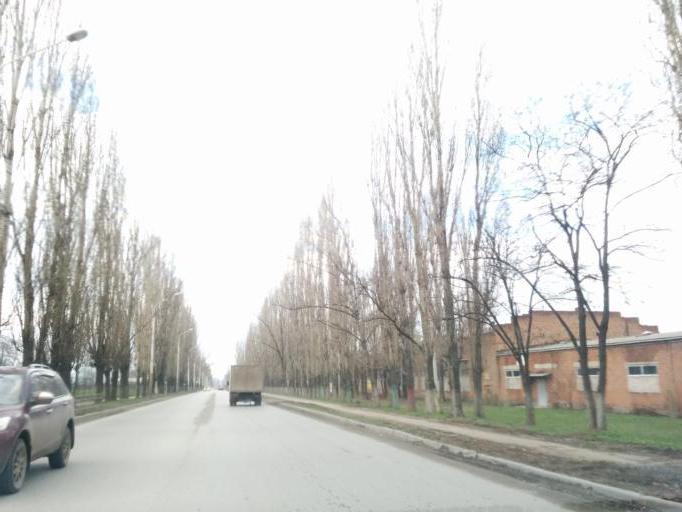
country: RU
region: Rostov
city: Shakhty
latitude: 47.6909
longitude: 40.2526
